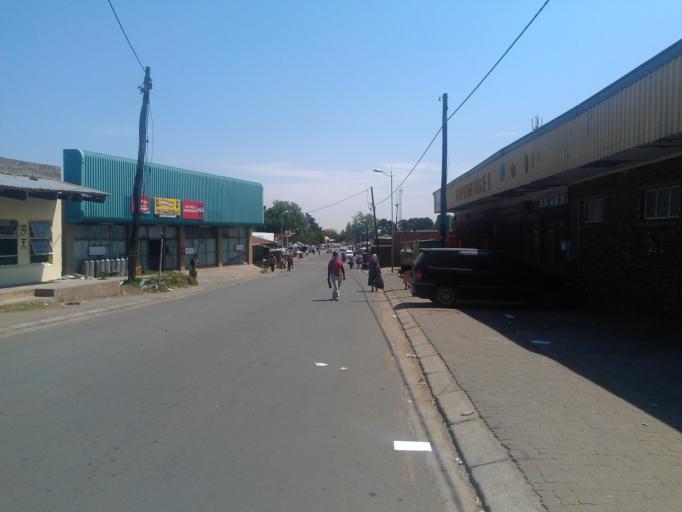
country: LS
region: Berea
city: Teyateyaneng
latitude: -29.1519
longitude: 27.7429
